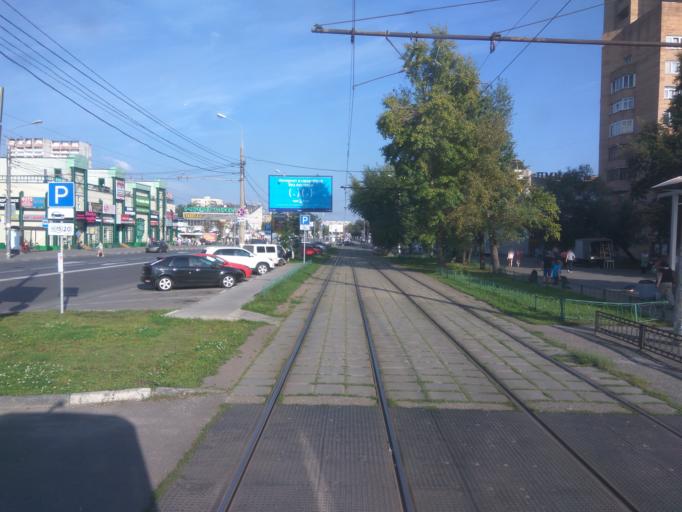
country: RU
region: Moskovskaya
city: Novogireyevo
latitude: 55.7519
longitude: 37.8147
